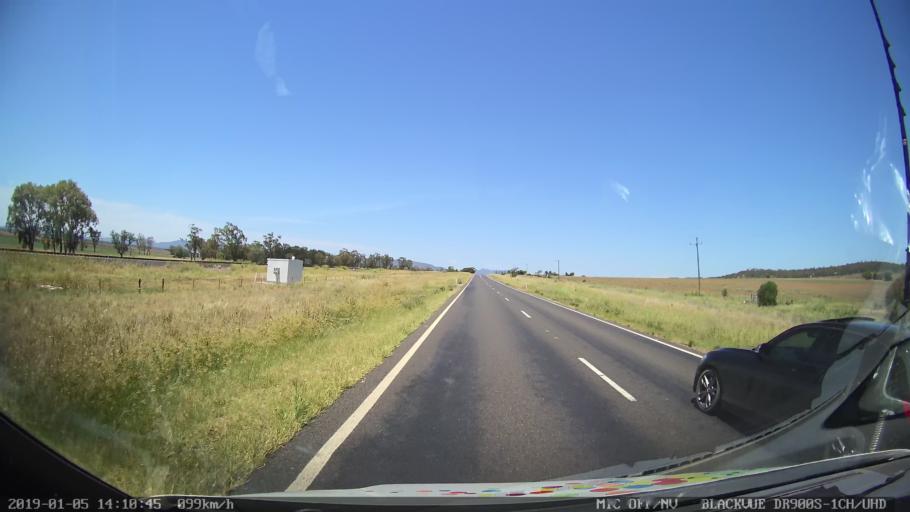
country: AU
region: New South Wales
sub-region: Gunnedah
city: Gunnedah
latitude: -31.2451
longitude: 150.4475
